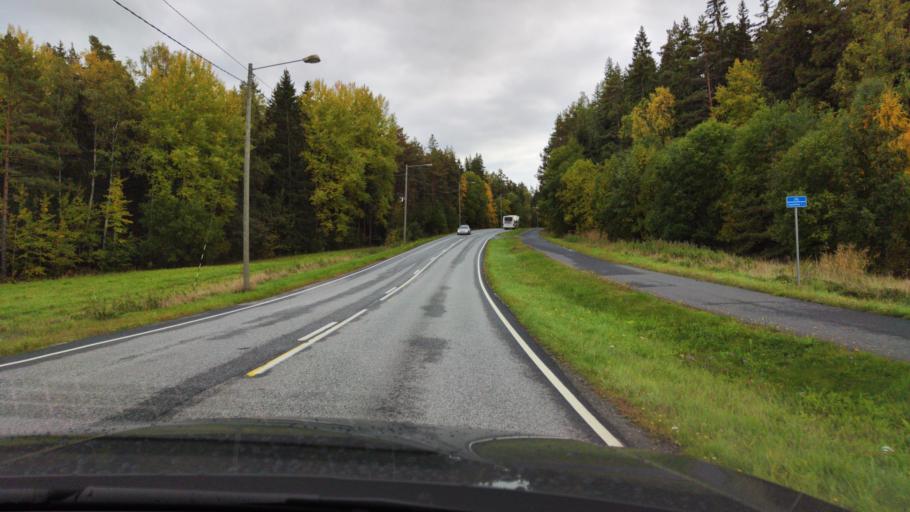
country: FI
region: Varsinais-Suomi
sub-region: Turku
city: Raisio
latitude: 60.3642
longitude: 22.1784
